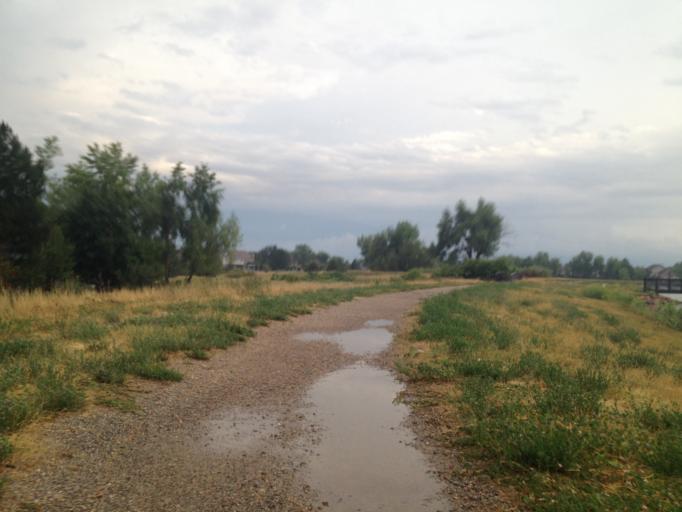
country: US
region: Colorado
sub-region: Boulder County
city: Louisville
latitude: 39.9822
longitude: -105.1612
